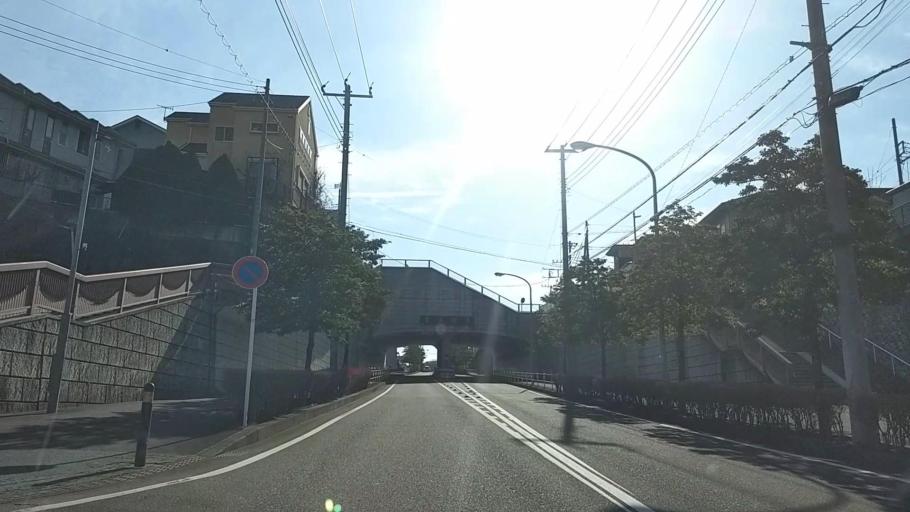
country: JP
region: Kanagawa
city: Hadano
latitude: 35.3658
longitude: 139.2263
